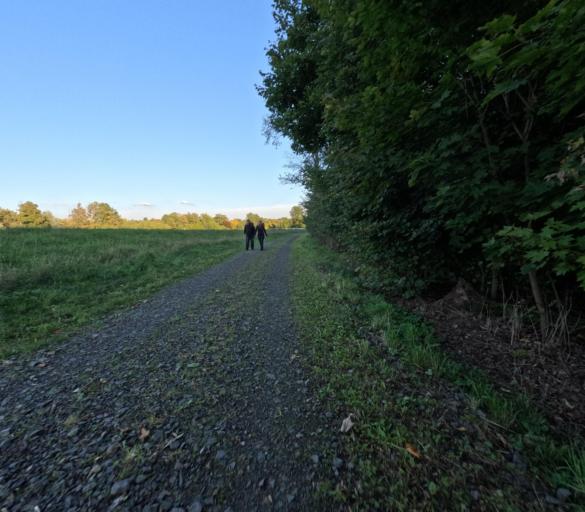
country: DE
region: Saxony
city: Leipzig
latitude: 51.3713
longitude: 12.3039
